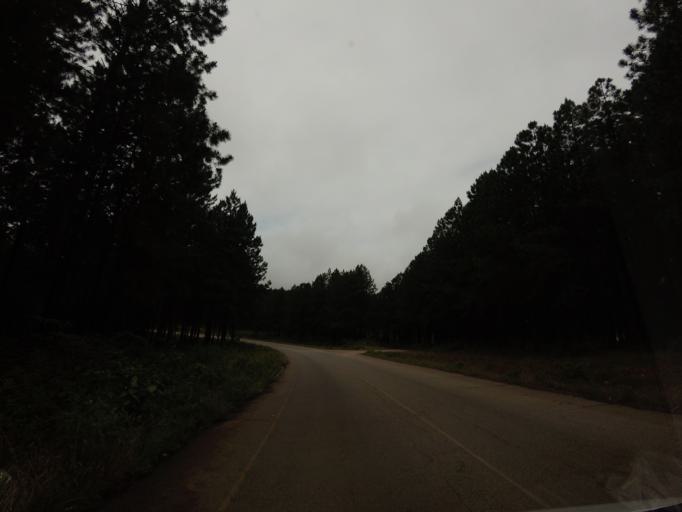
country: SZ
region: Hhohho
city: Piggs Peak
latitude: -25.9993
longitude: 31.2515
